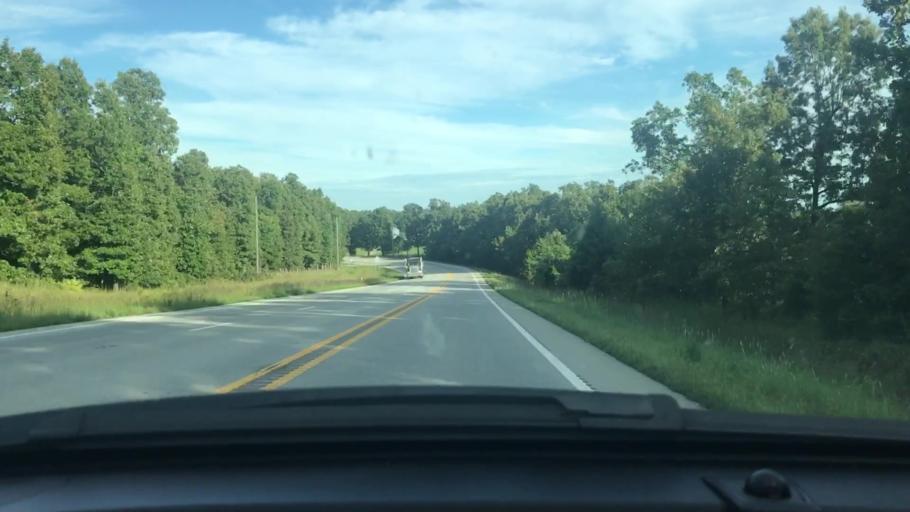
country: US
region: Arkansas
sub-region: Sharp County
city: Cherokee Village
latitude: 36.2726
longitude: -91.3721
